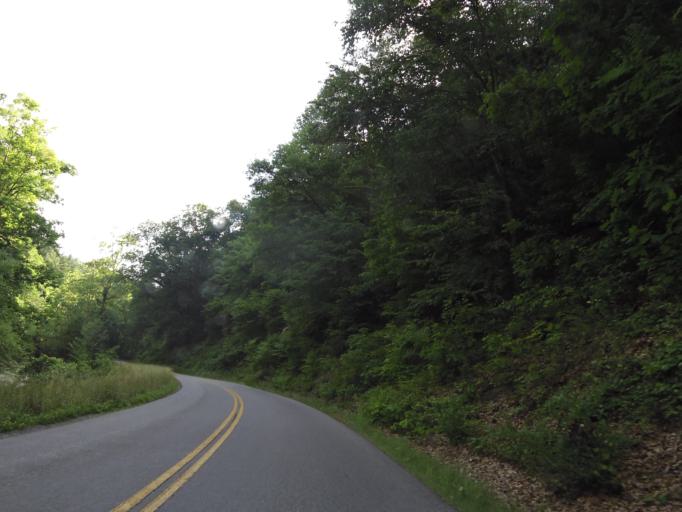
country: US
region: Tennessee
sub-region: Sevier County
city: Pigeon Forge
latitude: 35.6721
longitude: -83.6723
